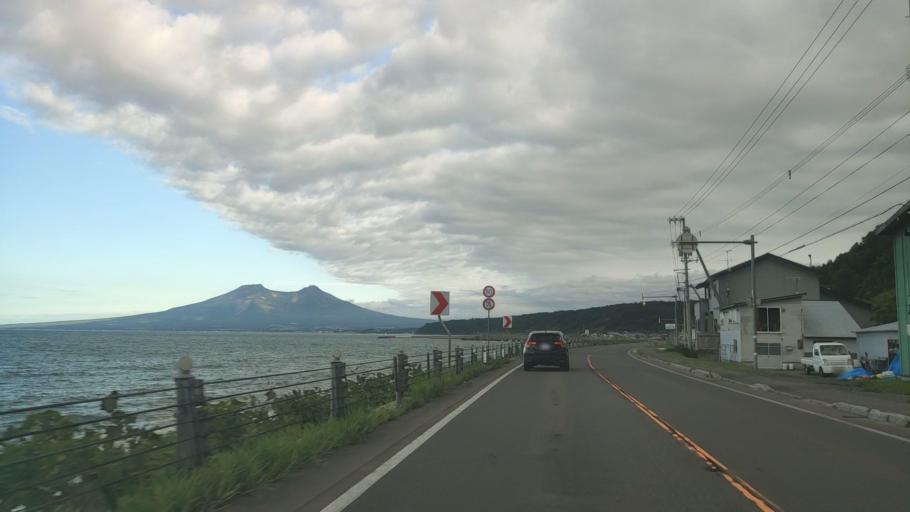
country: JP
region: Hokkaido
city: Nanae
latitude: 42.1406
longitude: 140.5035
